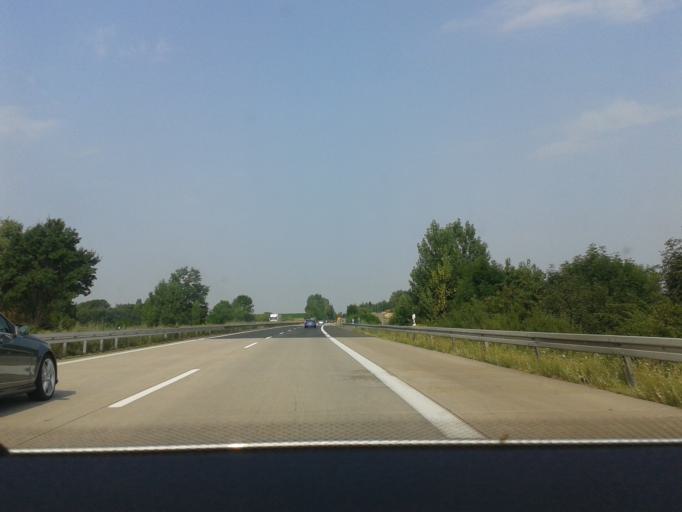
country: DE
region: Saxony
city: Dobeln
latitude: 51.1595
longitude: 13.1073
